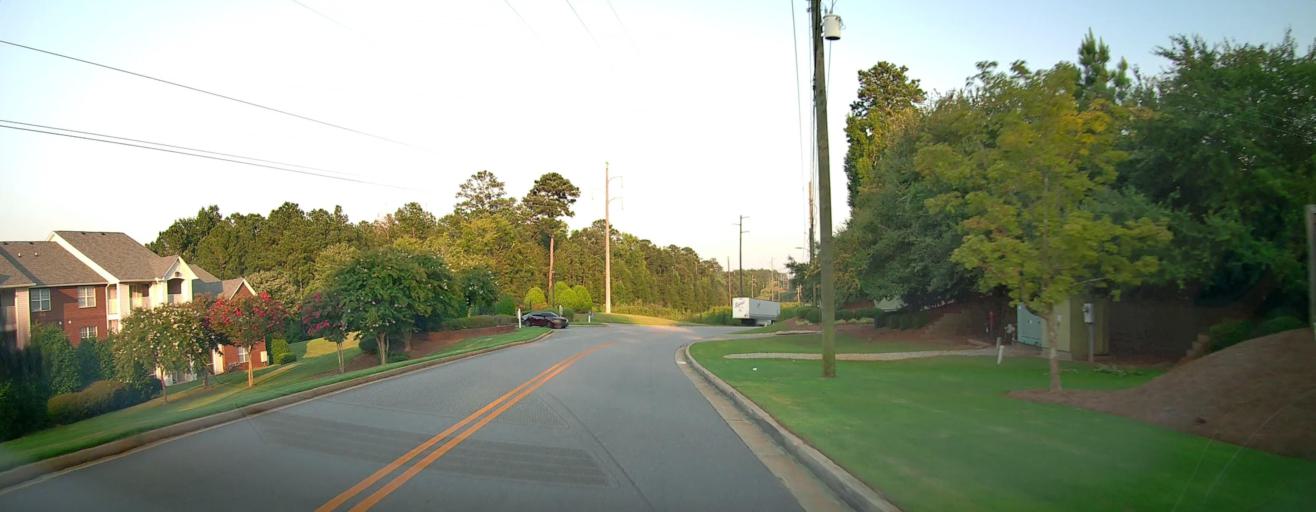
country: US
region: Georgia
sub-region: Bibb County
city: Macon
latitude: 32.9179
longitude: -83.7192
